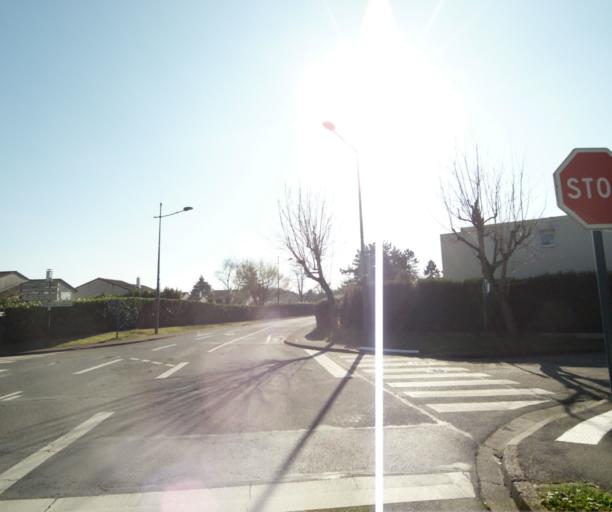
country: FR
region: Ile-de-France
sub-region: Departement du Val-d'Oise
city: Cergy
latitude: 49.0292
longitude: 2.0874
